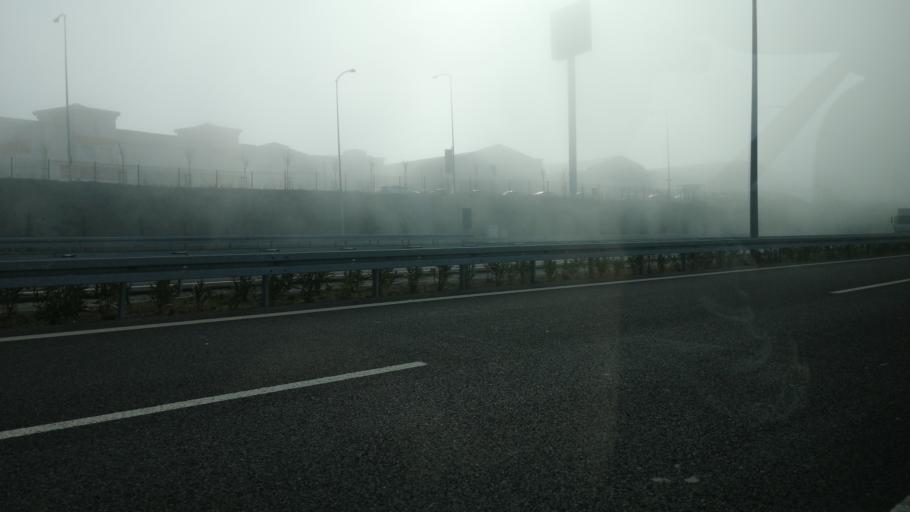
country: TR
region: Kocaeli
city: Tavsanli
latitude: 40.7742
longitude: 29.5184
